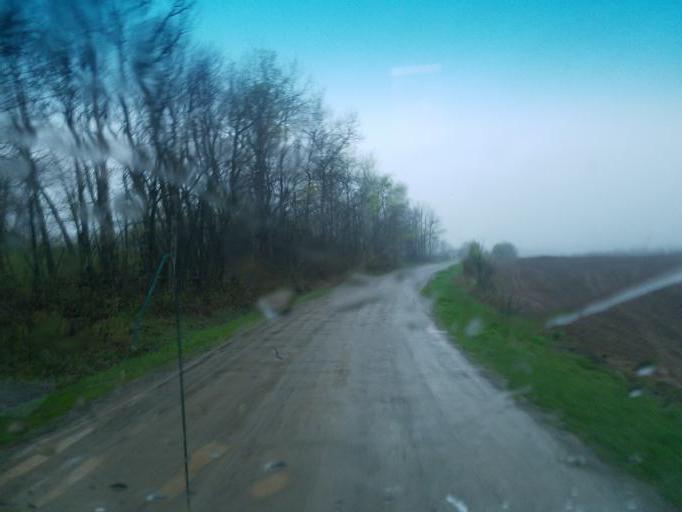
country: US
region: Pennsylvania
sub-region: Tioga County
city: Westfield
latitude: 41.9210
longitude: -77.7248
